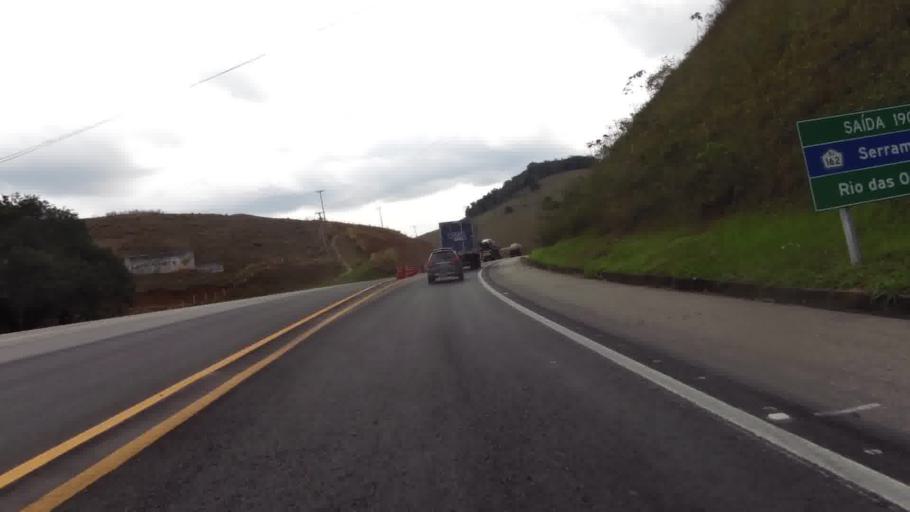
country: BR
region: Rio de Janeiro
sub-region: Casimiro De Abreu
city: Casimiro de Abreu
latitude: -22.4645
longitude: -42.0676
